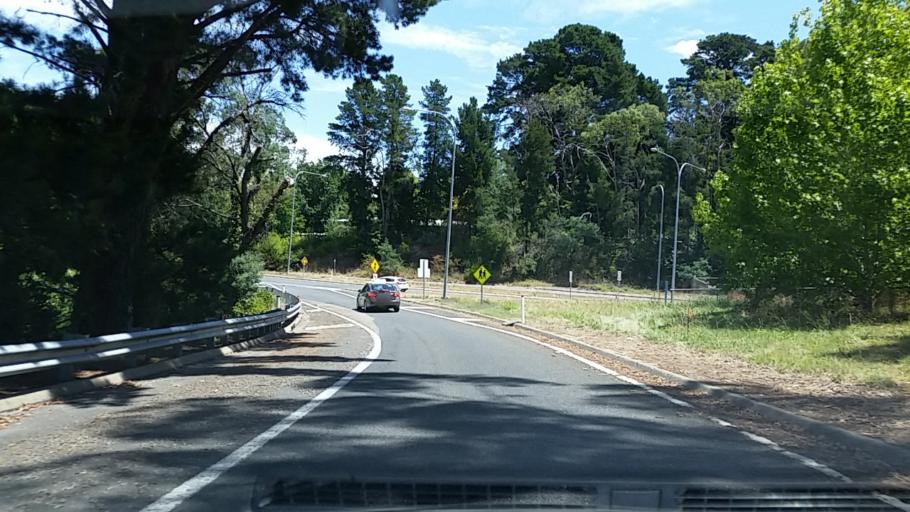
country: AU
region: South Australia
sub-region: Adelaide Hills
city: Heathfield
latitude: -35.0024
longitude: 138.7166
